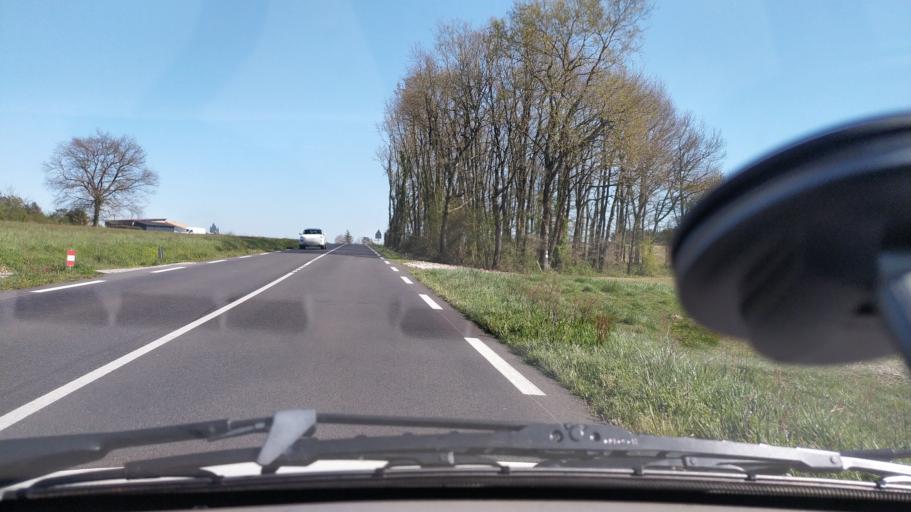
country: FR
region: Midi-Pyrenees
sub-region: Departement du Gers
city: Nogaro
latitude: 43.7490
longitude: -0.0657
